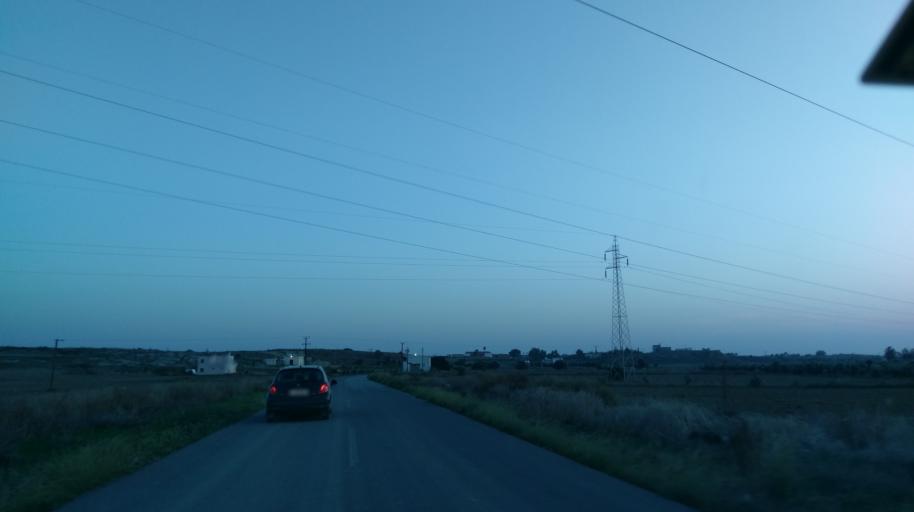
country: CY
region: Ammochostos
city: Trikomo
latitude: 35.2975
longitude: 33.8911
